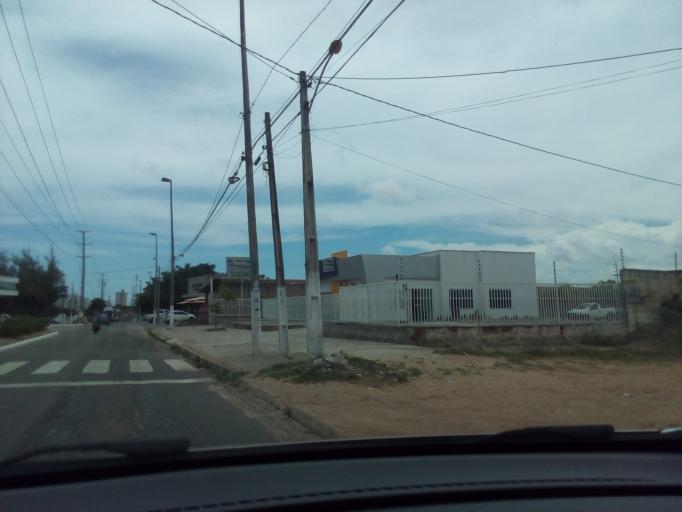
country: BR
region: Rio Grande do Norte
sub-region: Natal
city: Natal
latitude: -5.8426
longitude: -35.2201
